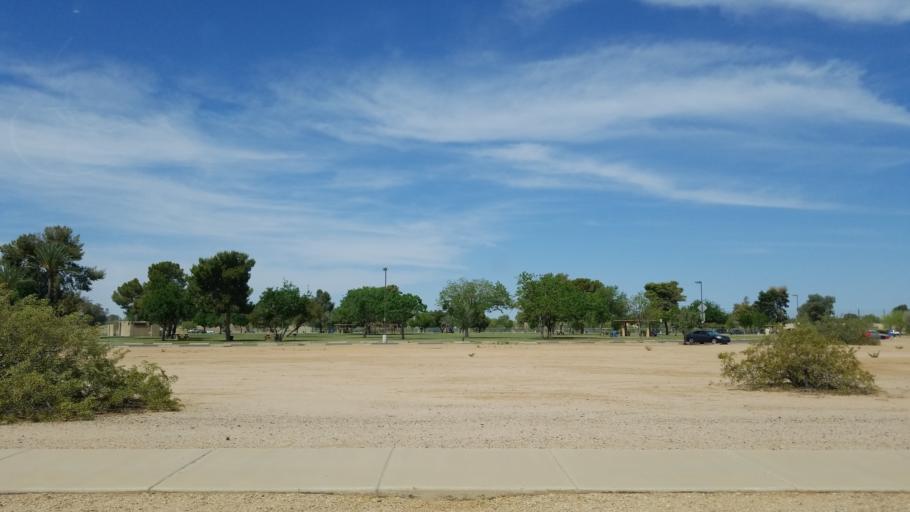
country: US
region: Arizona
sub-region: Maricopa County
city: Paradise Valley
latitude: 33.6495
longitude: -111.9963
